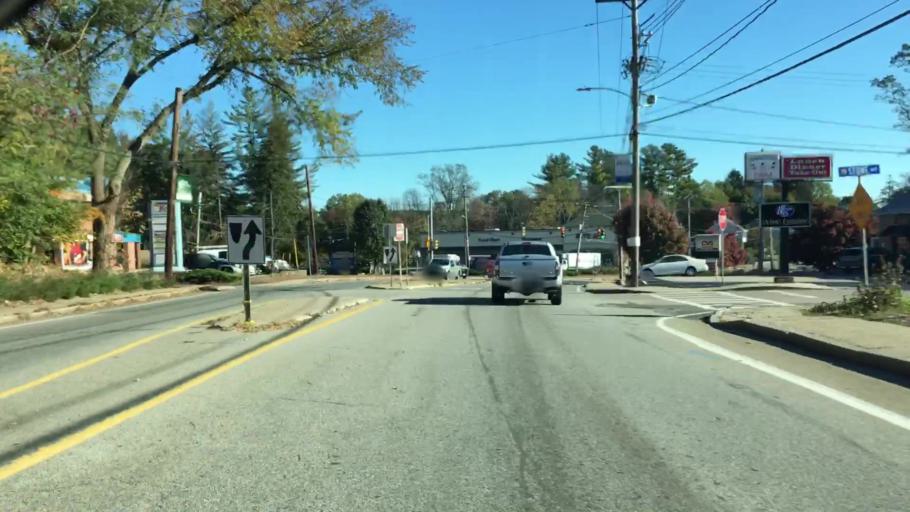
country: US
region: Massachusetts
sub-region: Middlesex County
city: Ashland
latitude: 42.2549
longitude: -71.4679
